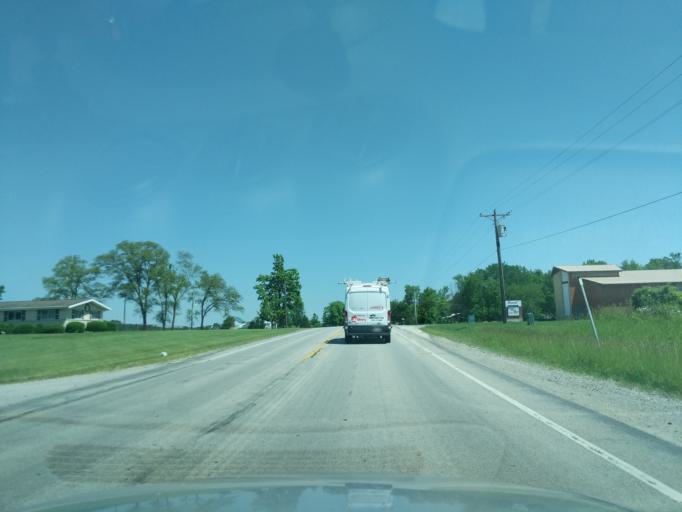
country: US
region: Indiana
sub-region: Whitley County
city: Columbia City
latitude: 41.1790
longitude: -85.4915
